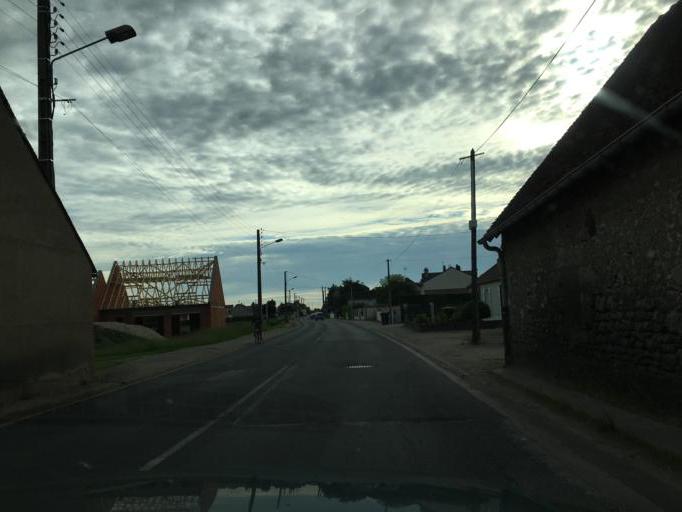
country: FR
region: Centre
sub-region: Departement du Loiret
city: Chaingy
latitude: 47.8876
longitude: 1.7821
